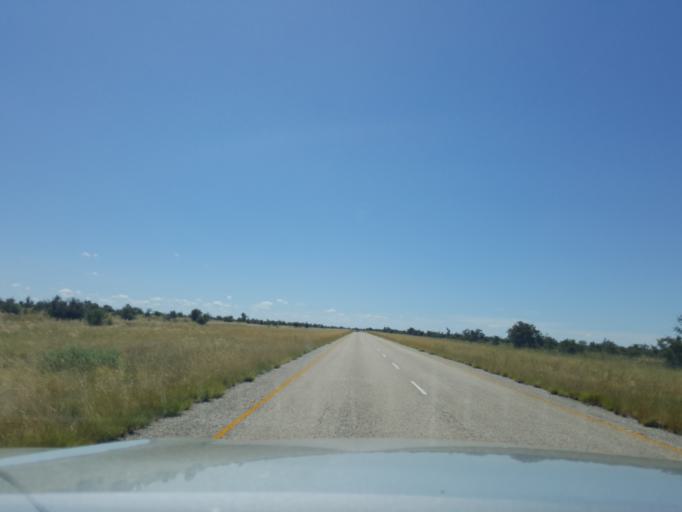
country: BW
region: Central
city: Gweta
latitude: -20.2167
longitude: 25.0749
